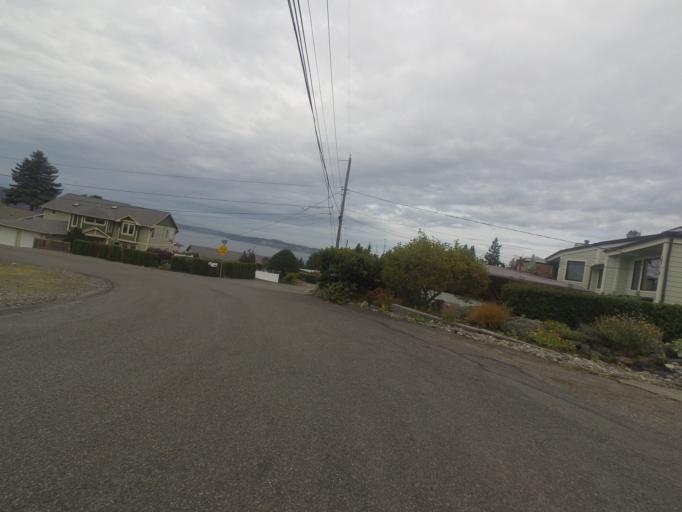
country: US
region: Washington
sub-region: Pierce County
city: University Place
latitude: 47.2149
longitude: -122.5690
